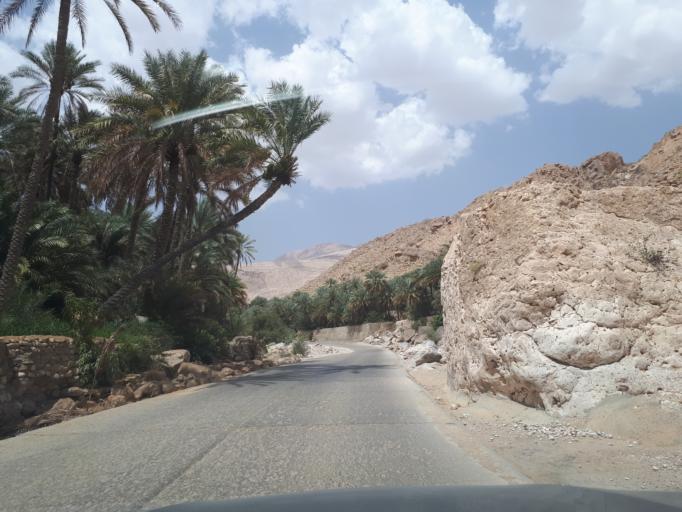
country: OM
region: Ash Sharqiyah
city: Badiyah
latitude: 22.6077
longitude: 59.0903
